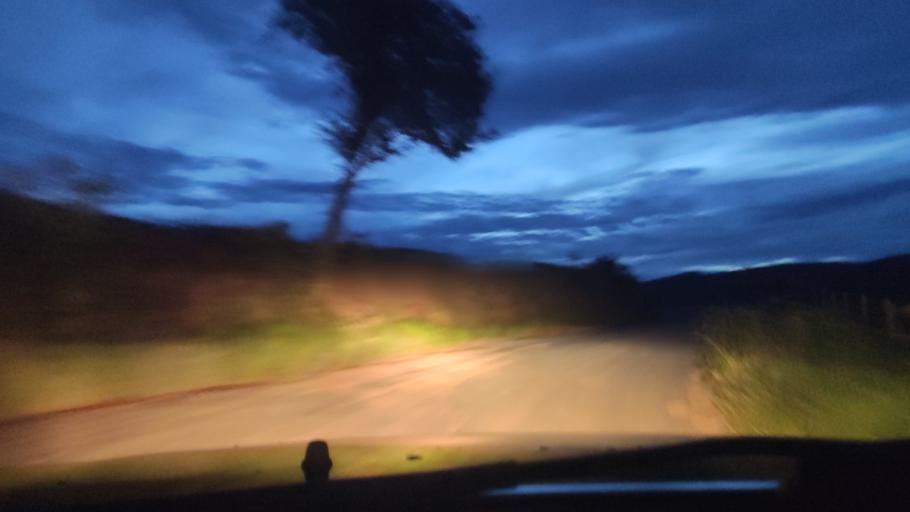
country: BR
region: Sao Paulo
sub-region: Aguas De Lindoia
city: Aguas de Lindoia
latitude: -22.5561
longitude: -46.6174
